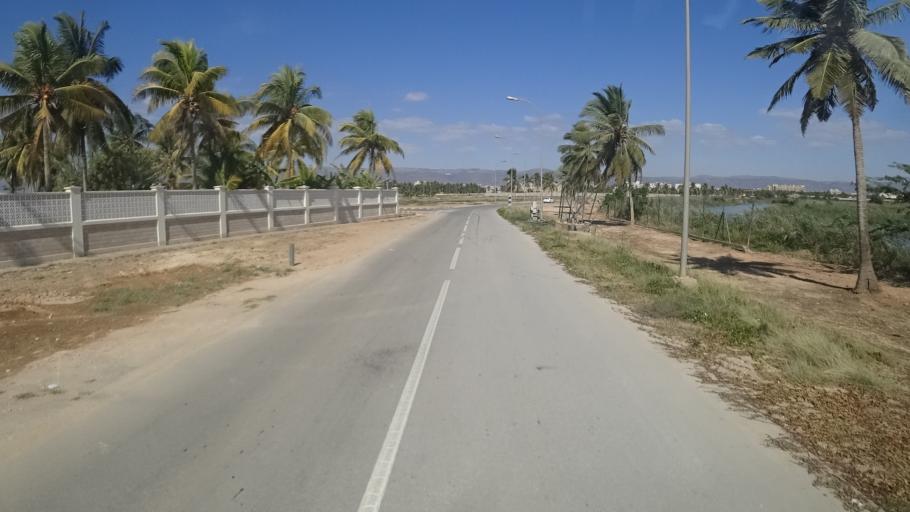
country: OM
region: Zufar
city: Salalah
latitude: 16.9959
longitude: 54.0656
